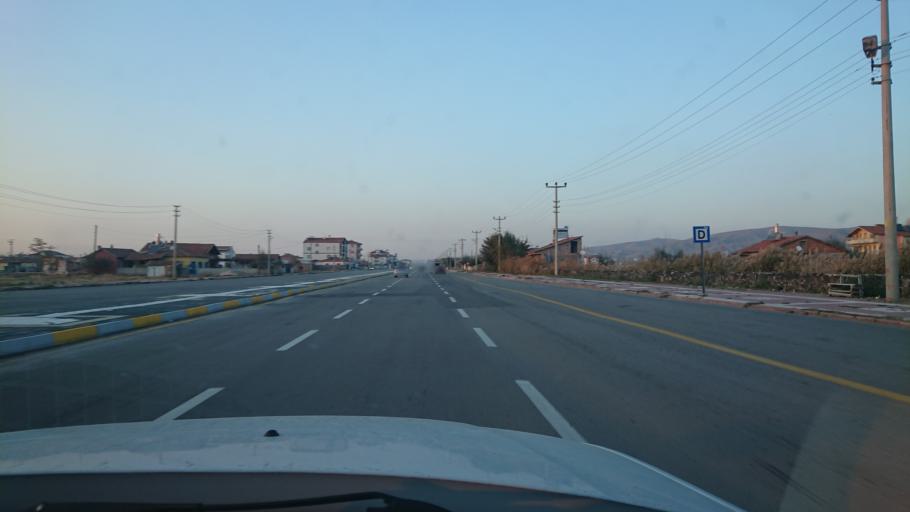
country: TR
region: Aksaray
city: Aksaray
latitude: 38.3332
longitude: 34.0499
